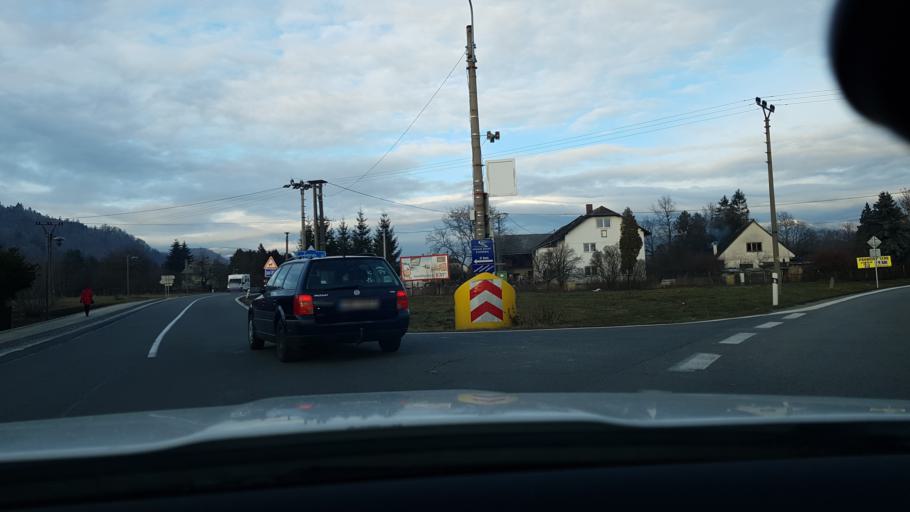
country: CZ
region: Olomoucky
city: Rapotin
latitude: 50.0012
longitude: 17.0189
